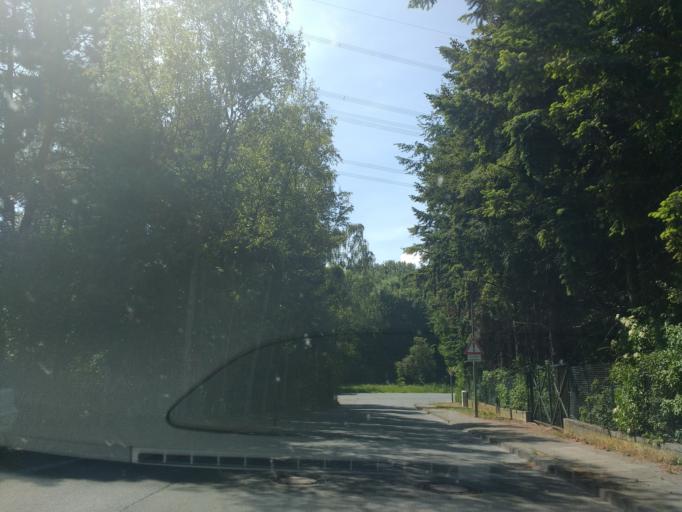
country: DE
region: North Rhine-Westphalia
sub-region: Regierungsbezirk Detmold
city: Paderborn
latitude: 51.6942
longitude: 8.7112
